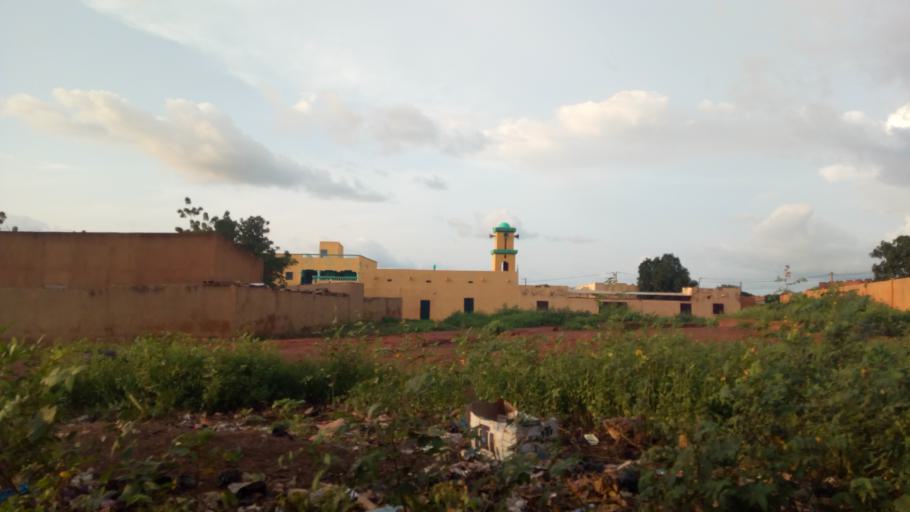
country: ML
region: Sikasso
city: Koutiala
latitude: 12.3747
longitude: -5.4814
